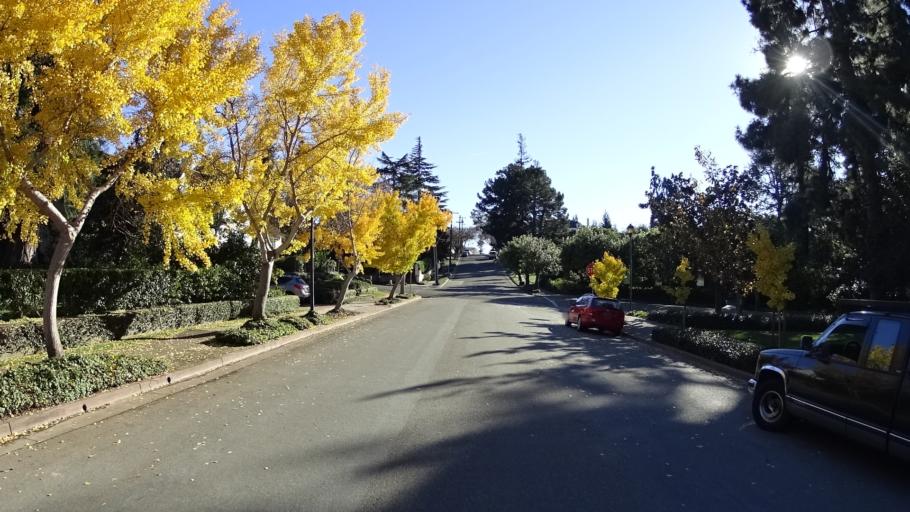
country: US
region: California
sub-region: Alameda County
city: Piedmont
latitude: 37.8186
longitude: -122.2240
